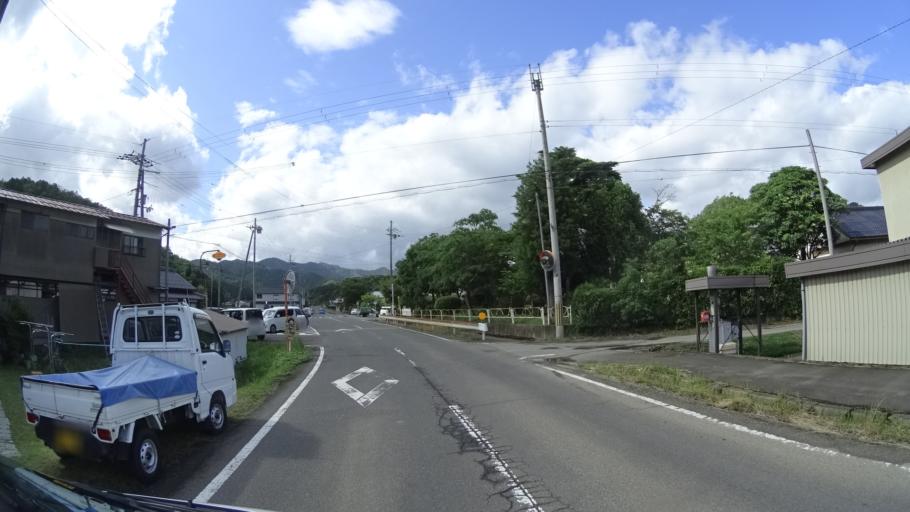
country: JP
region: Kyoto
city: Ayabe
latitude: 35.3703
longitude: 135.2408
